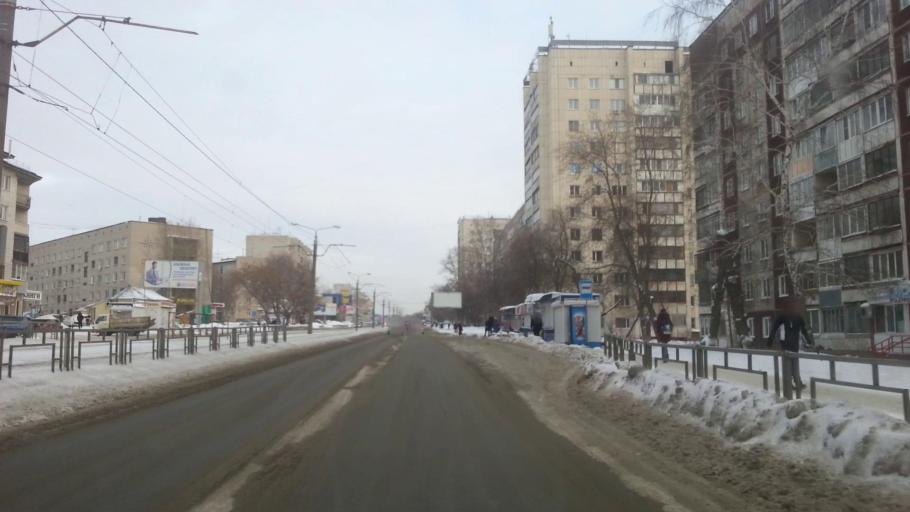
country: RU
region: Altai Krai
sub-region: Gorod Barnaulskiy
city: Barnaul
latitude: 53.3705
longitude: 83.7427
